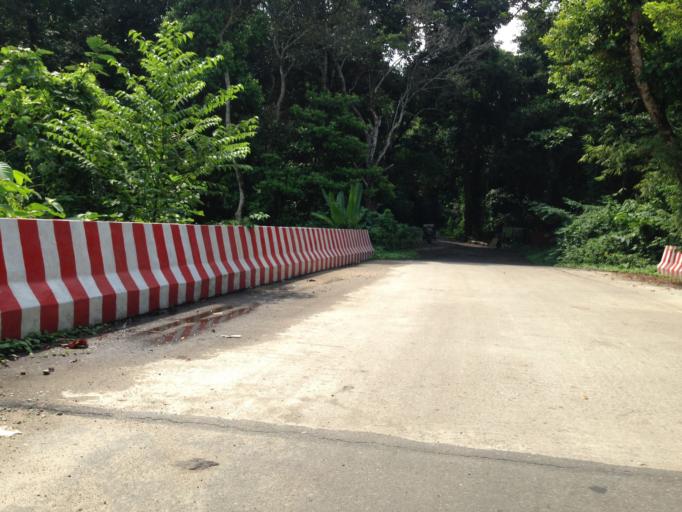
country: IN
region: Tripura
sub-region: Dhalai
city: Kamalpur
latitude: 24.3135
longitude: 91.7741
